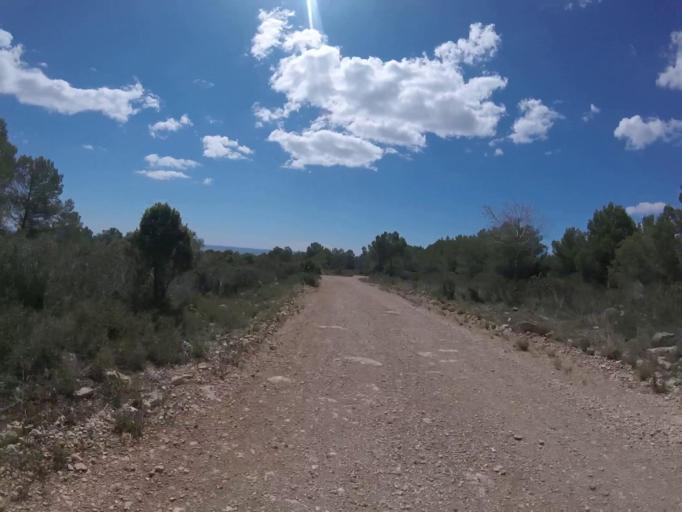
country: ES
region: Valencia
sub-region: Provincia de Castello
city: Alcoceber
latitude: 40.2872
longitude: 0.3196
